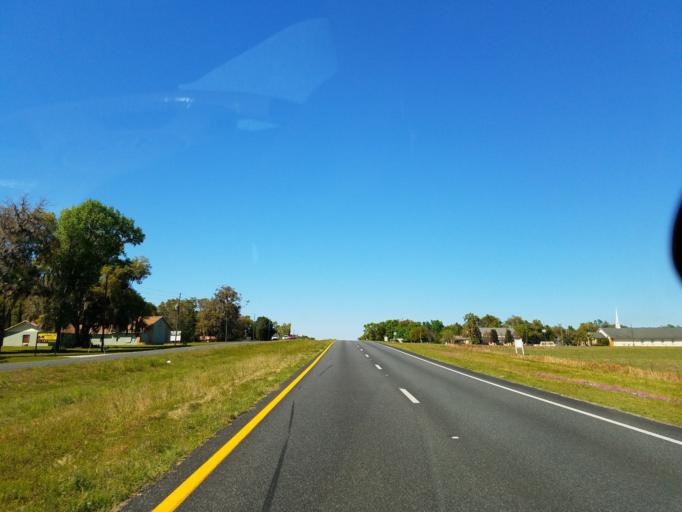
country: US
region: Florida
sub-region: Marion County
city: Belleview
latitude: 29.0405
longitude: -82.0451
